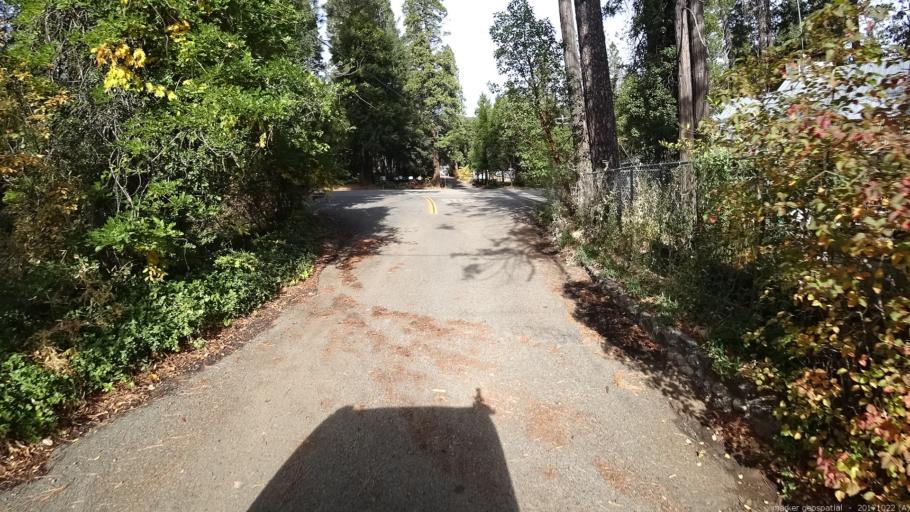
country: US
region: California
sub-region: Siskiyou County
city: Dunsmuir
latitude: 41.0733
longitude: -122.3604
